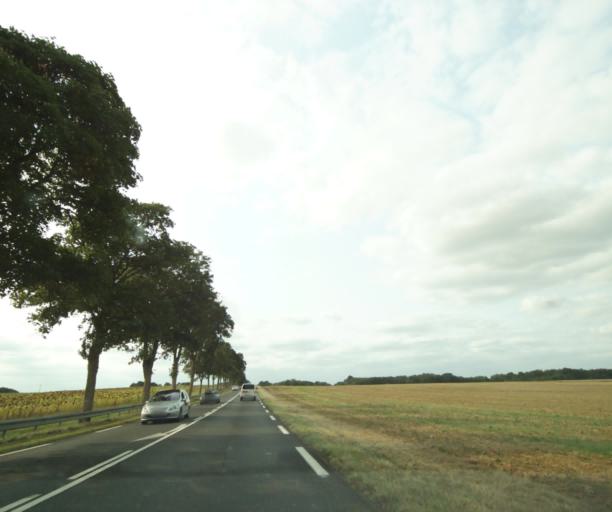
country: FR
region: Centre
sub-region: Departement d'Indre-et-Loire
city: Reignac-sur-Indre
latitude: 47.2274
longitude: 0.8794
